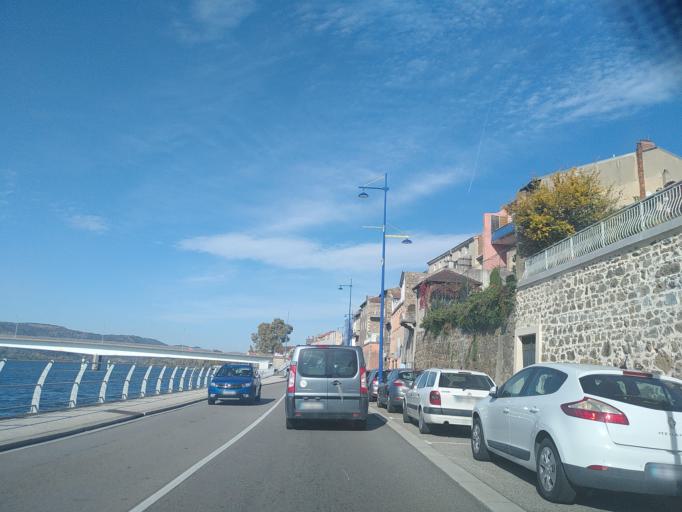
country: FR
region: Rhone-Alpes
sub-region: Departement de la Drome
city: Saint-Vallier
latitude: 45.1822
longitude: 4.8139
